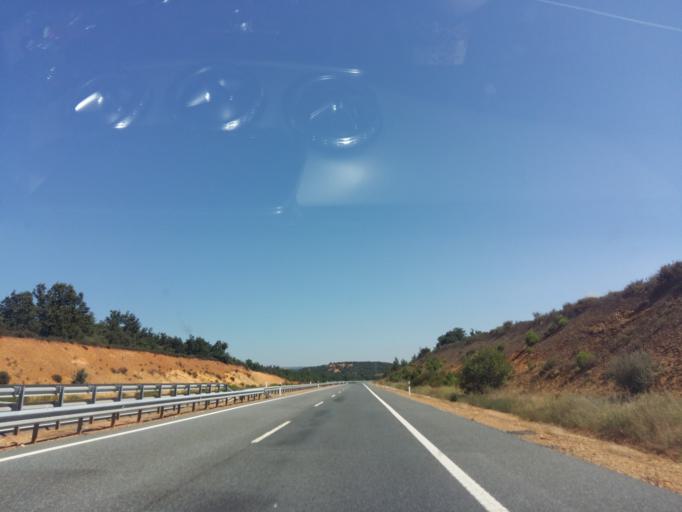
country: ES
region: Castille and Leon
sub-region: Provincia de Leon
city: San Justo de la Vega
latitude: 42.4475
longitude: -5.9800
